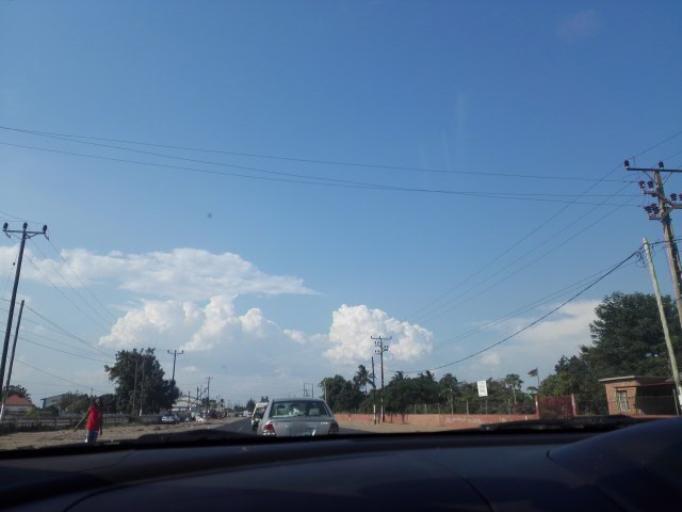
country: MZ
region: Maputo City
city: Maputo
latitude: -25.8591
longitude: 32.5668
